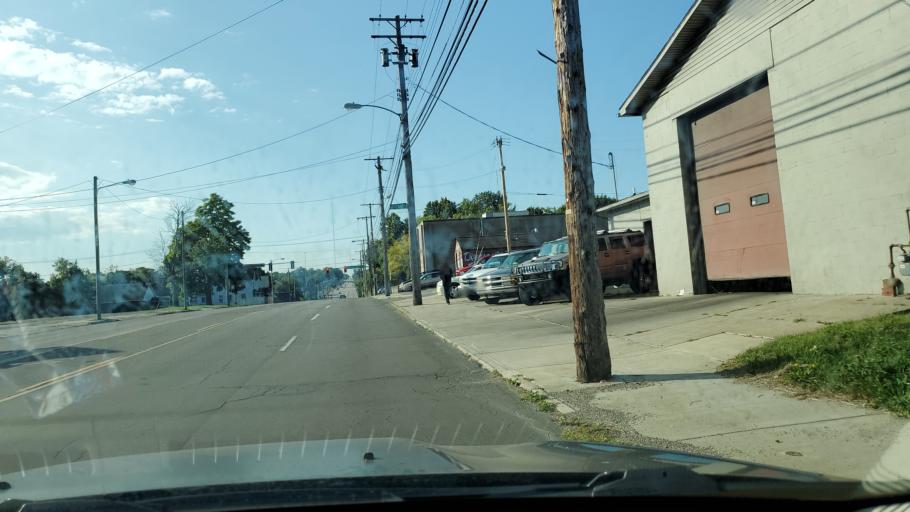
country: US
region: Ohio
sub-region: Mahoning County
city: Youngstown
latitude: 41.0877
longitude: -80.6464
